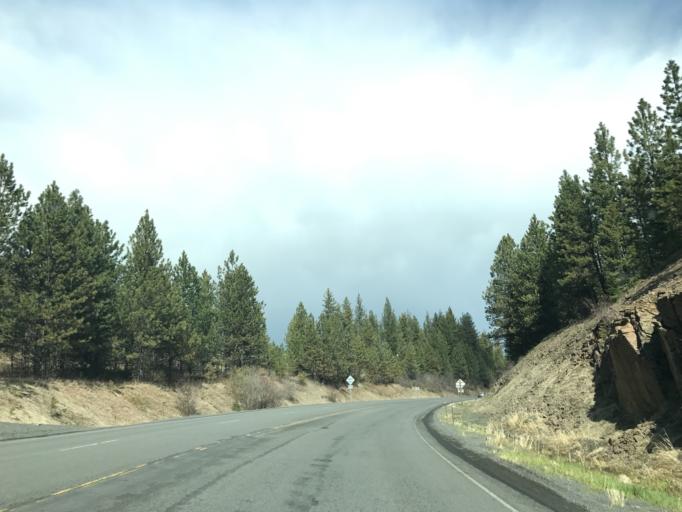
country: US
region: Idaho
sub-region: Idaho County
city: Grangeville
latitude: 45.8468
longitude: -116.2393
